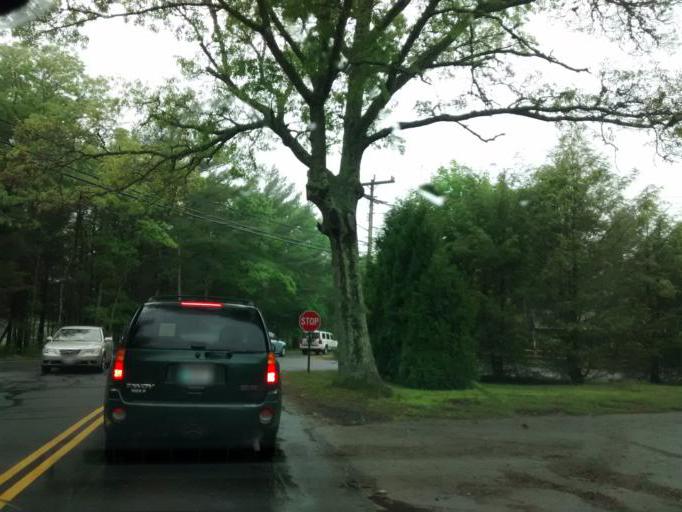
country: US
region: Massachusetts
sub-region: Barnstable County
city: Pocasset
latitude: 41.6889
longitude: -70.6001
